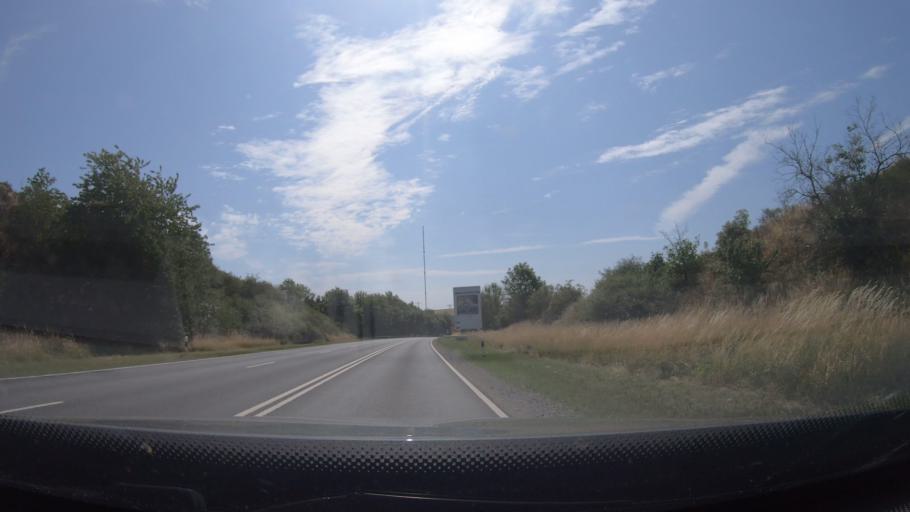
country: LU
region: Diekirch
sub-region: Canton de Clervaux
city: Hosingen
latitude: 50.0287
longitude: 6.0868
